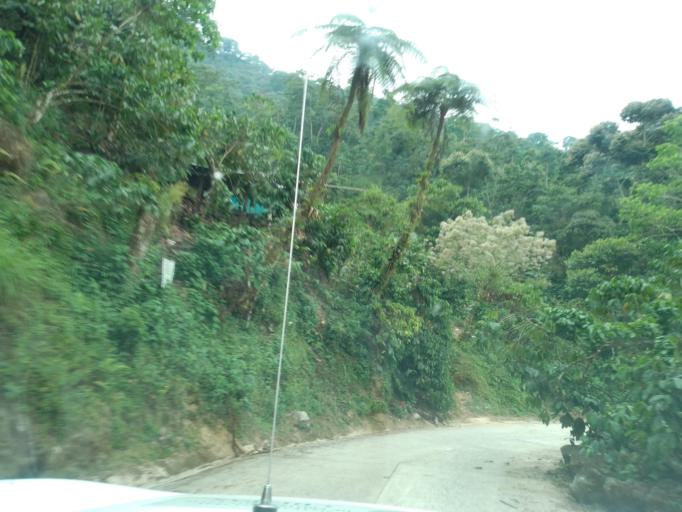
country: MX
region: Chiapas
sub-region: Union Juarez
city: Santo Domingo
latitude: 15.0572
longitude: -92.1106
